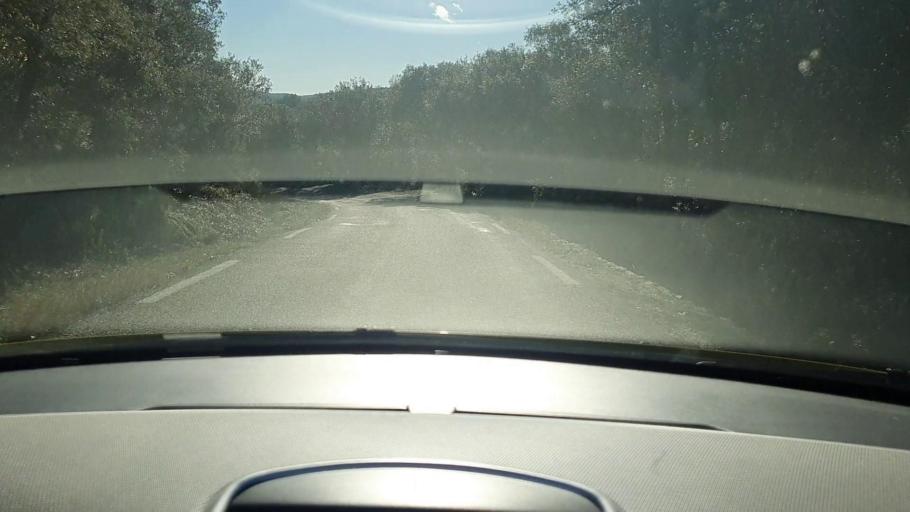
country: FR
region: Languedoc-Roussillon
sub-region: Departement du Gard
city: Lasalle
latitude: 44.0738
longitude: 3.8280
